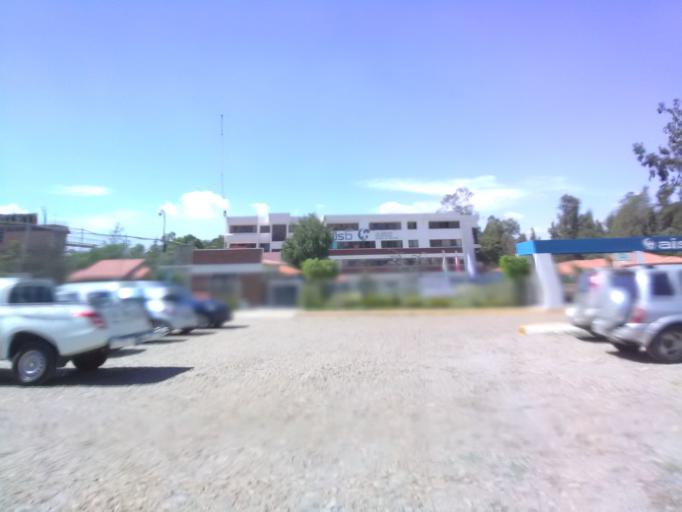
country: BO
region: Cochabamba
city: Cochabamba
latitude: -17.3546
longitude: -66.2018
